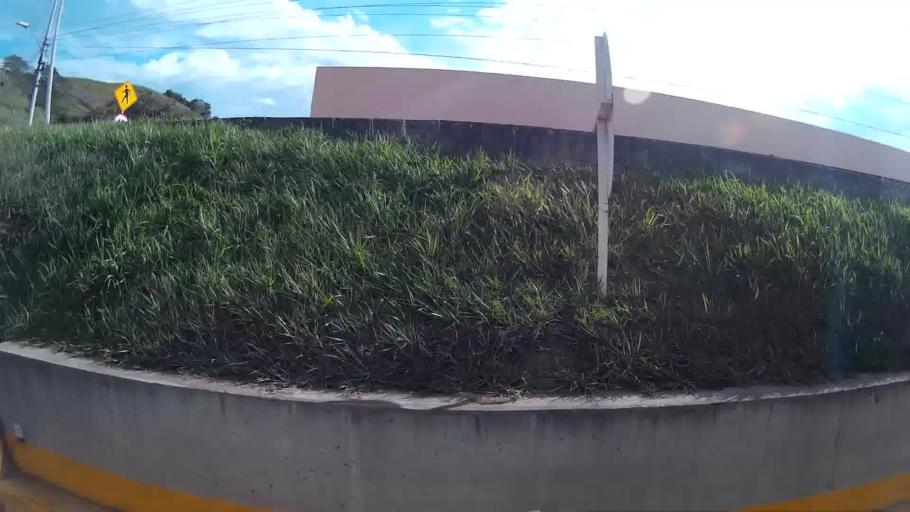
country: CO
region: Valle del Cauca
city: Cartago
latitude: 4.8012
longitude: -75.8422
